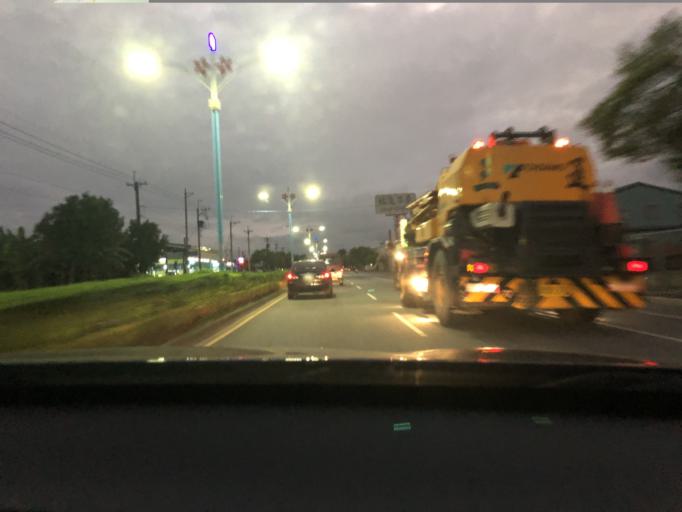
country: TW
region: Taiwan
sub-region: Hualien
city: Hualian
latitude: 23.9643
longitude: 121.5667
